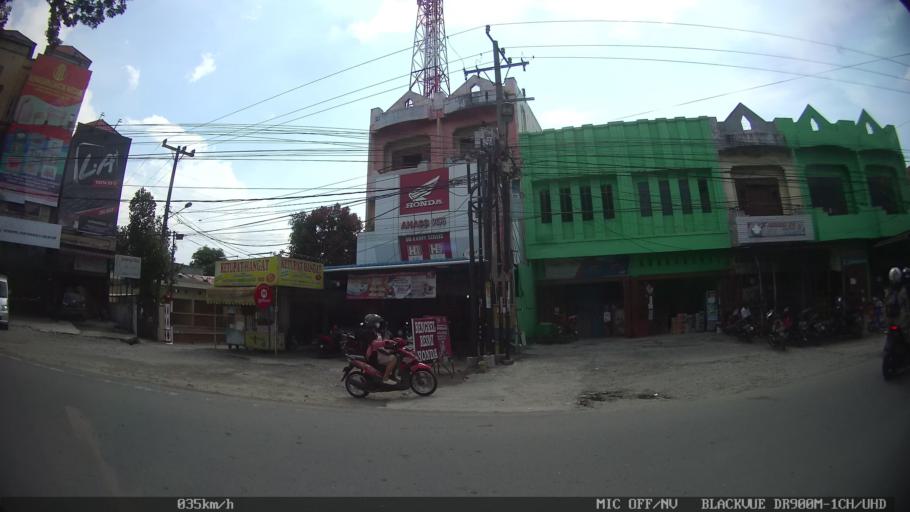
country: ID
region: North Sumatra
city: Medan
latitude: 3.6178
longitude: 98.6651
